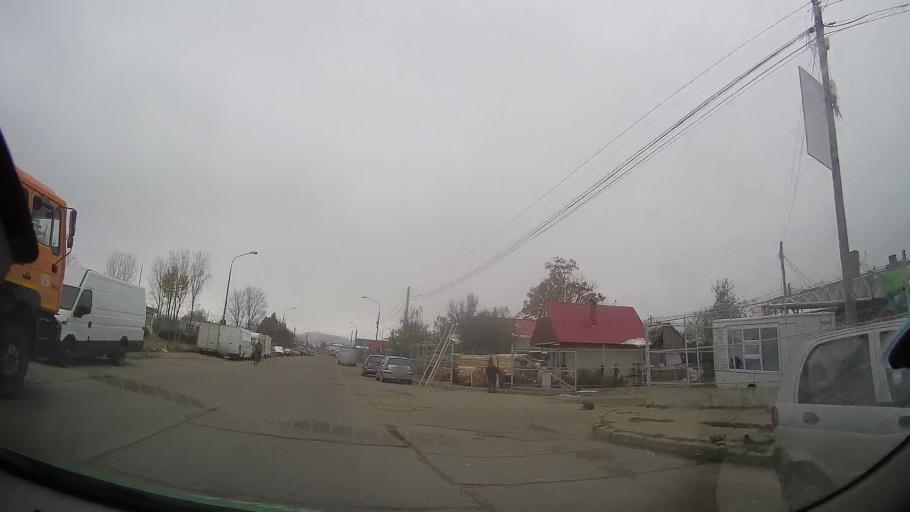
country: RO
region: Vaslui
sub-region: Municipiul Barlad
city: Barlad
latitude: 46.2382
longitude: 27.6776
